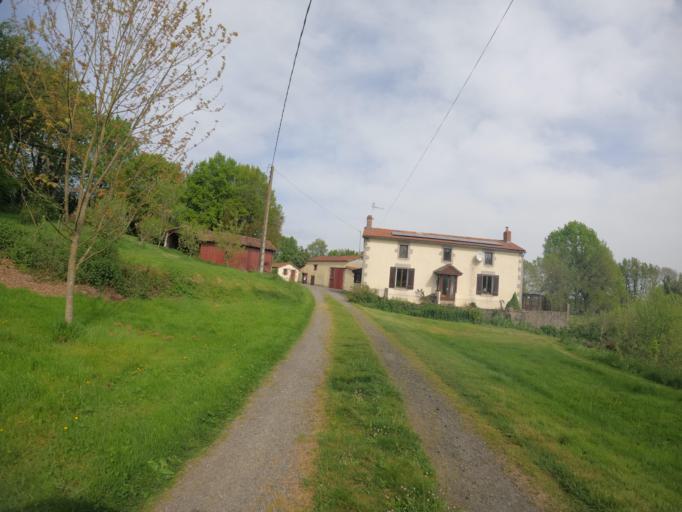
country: FR
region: Poitou-Charentes
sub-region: Departement des Deux-Sevres
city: La Chapelle-Saint-Laurent
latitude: 46.6958
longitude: -0.5093
